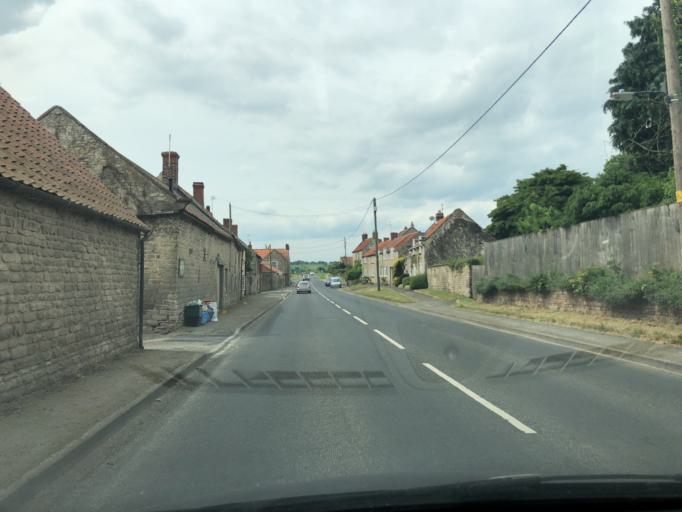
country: GB
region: England
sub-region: North Yorkshire
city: Pickering
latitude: 54.2611
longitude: -0.8109
